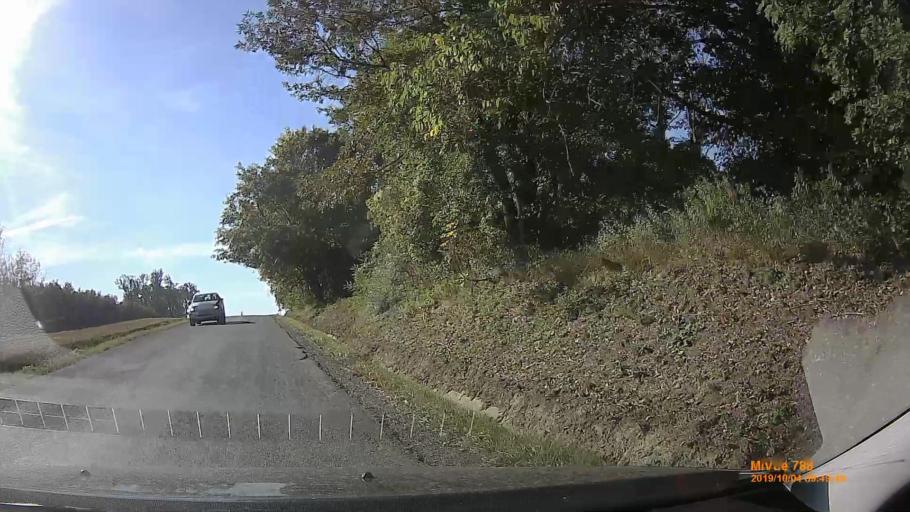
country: HU
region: Somogy
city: Kaposvar
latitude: 46.4416
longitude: 17.7697
